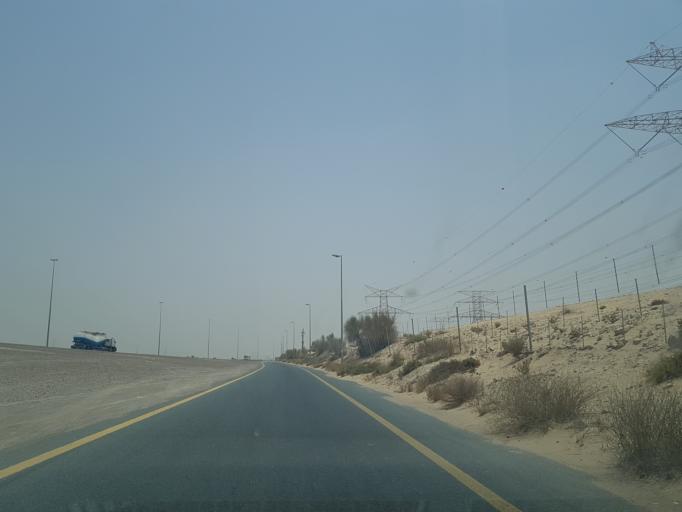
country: AE
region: Dubai
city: Dubai
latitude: 25.0598
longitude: 55.3238
